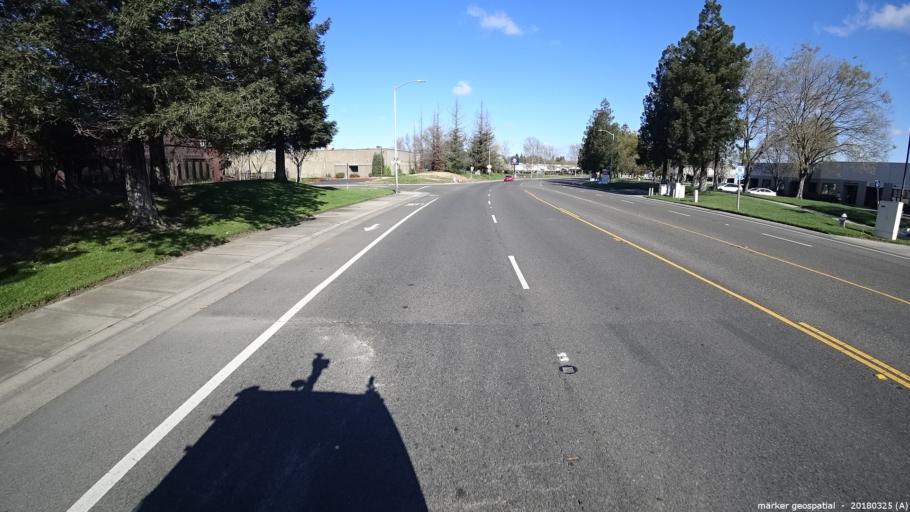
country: US
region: California
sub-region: Sacramento County
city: Rio Linda
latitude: 38.6515
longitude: -121.4772
